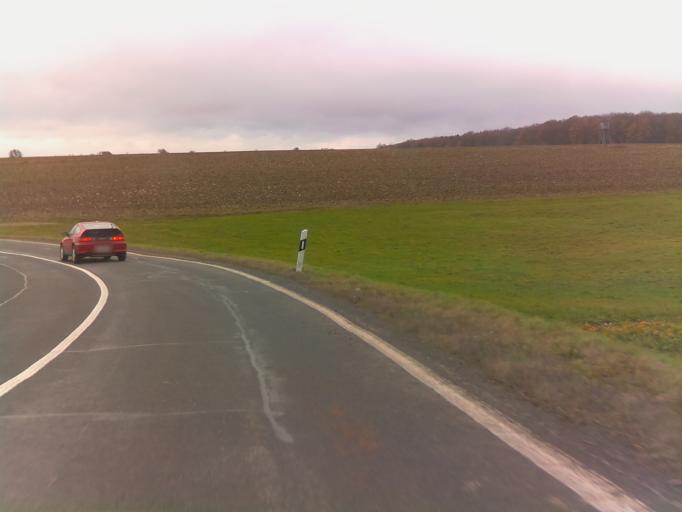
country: DE
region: Thuringia
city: Klettbach
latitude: 50.9190
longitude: 11.1741
